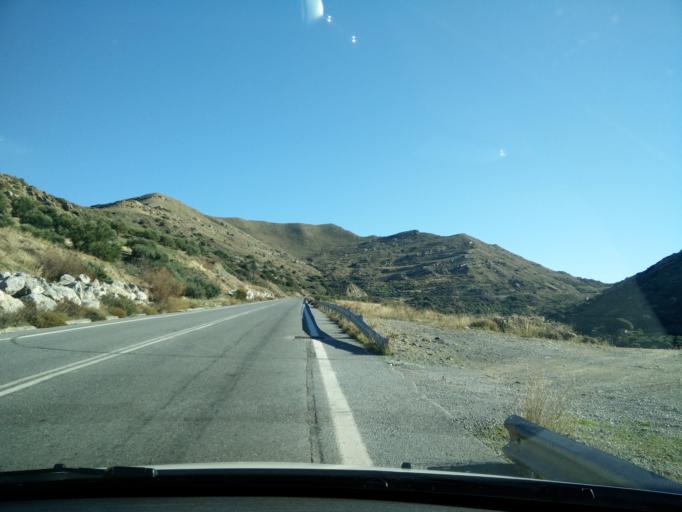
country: GR
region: Crete
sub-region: Nomos Irakleiou
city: Arkalochori
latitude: 35.0655
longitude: 25.3557
